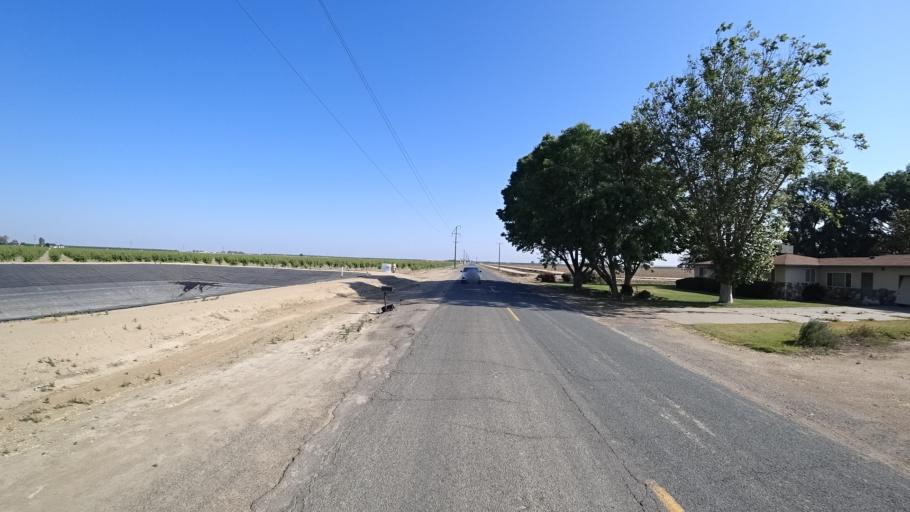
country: US
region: California
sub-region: Kings County
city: Home Garden
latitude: 36.2360
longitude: -119.5832
